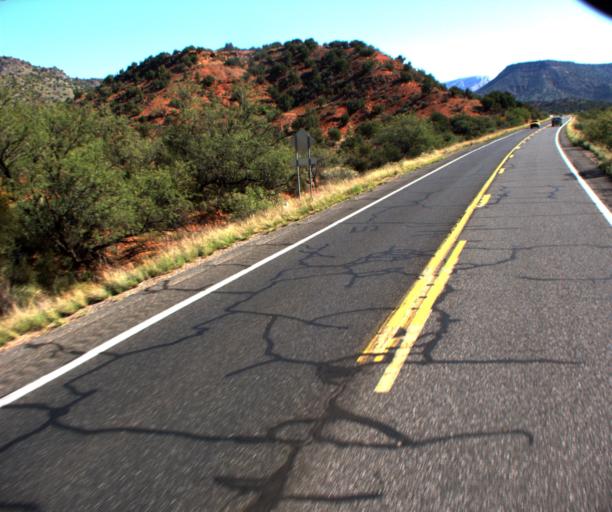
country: US
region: Arizona
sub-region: Yavapai County
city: Big Park
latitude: 34.7389
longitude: -111.7732
